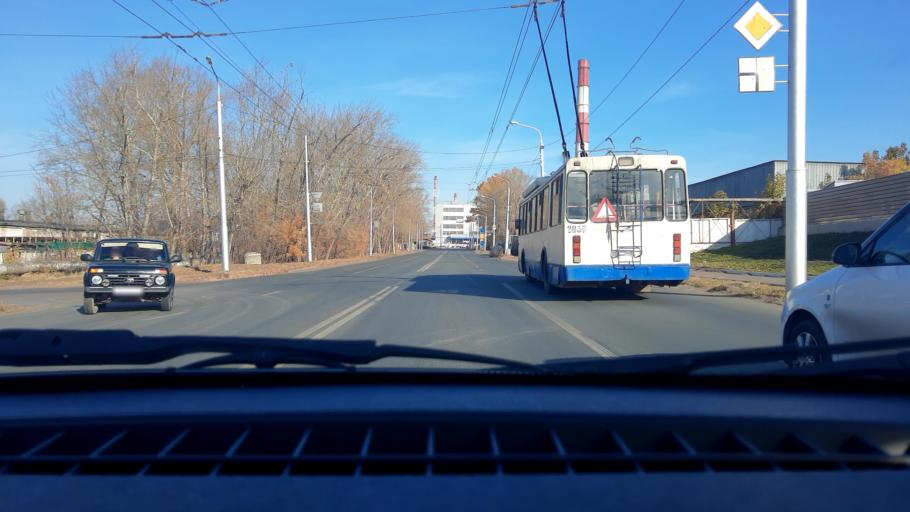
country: RU
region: Bashkortostan
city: Ufa
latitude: 54.8343
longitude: 56.0897
